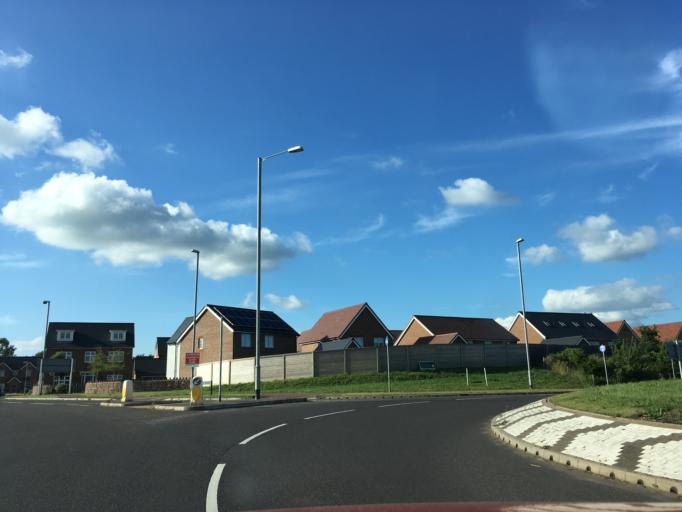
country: GB
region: England
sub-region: Somerset
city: Creech Saint Michael
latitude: 51.0308
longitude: -3.0577
